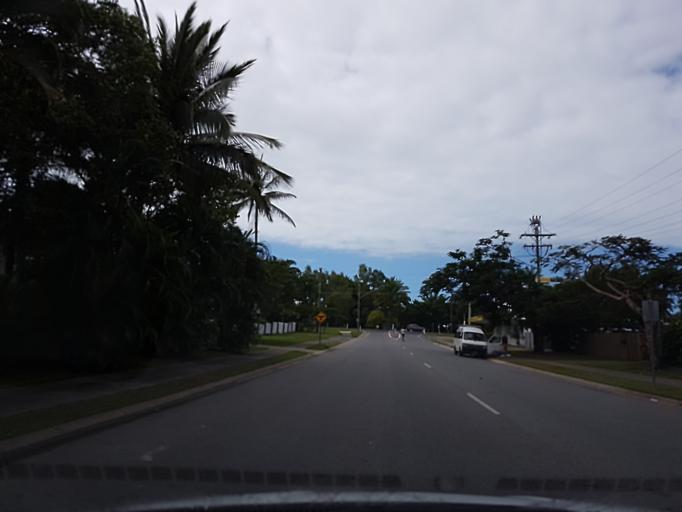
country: AU
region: Queensland
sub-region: Cairns
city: Port Douglas
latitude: -16.4924
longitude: 145.4632
